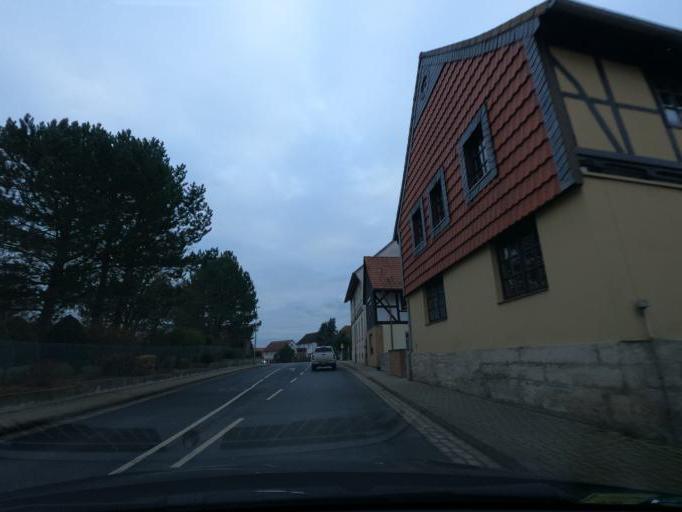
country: DE
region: Lower Saxony
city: Roklum
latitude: 52.0660
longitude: 10.7399
